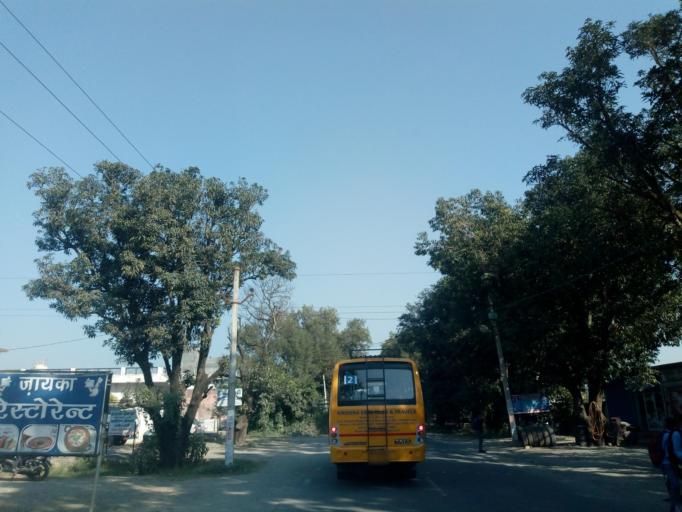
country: IN
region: Uttarakhand
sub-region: Dehradun
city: Harbatpur
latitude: 30.4414
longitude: 77.7279
